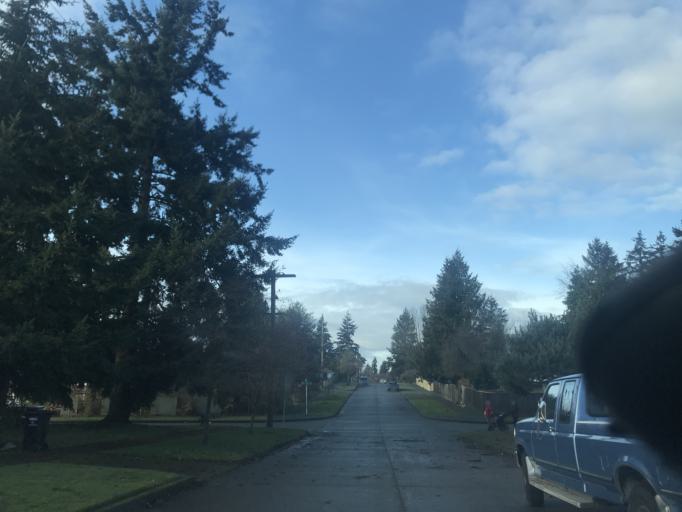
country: US
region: Washington
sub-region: King County
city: White Center
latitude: 47.5265
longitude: -122.3721
